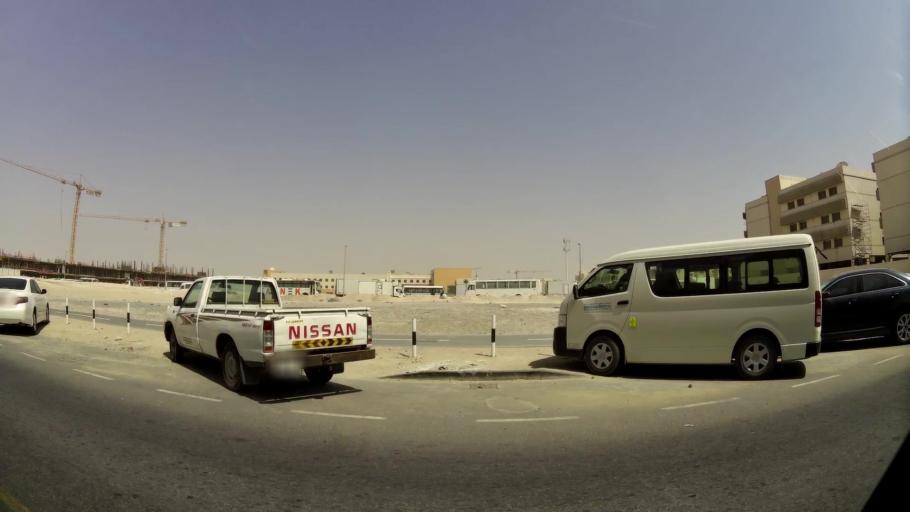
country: AE
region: Dubai
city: Dubai
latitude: 25.1539
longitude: 55.2466
